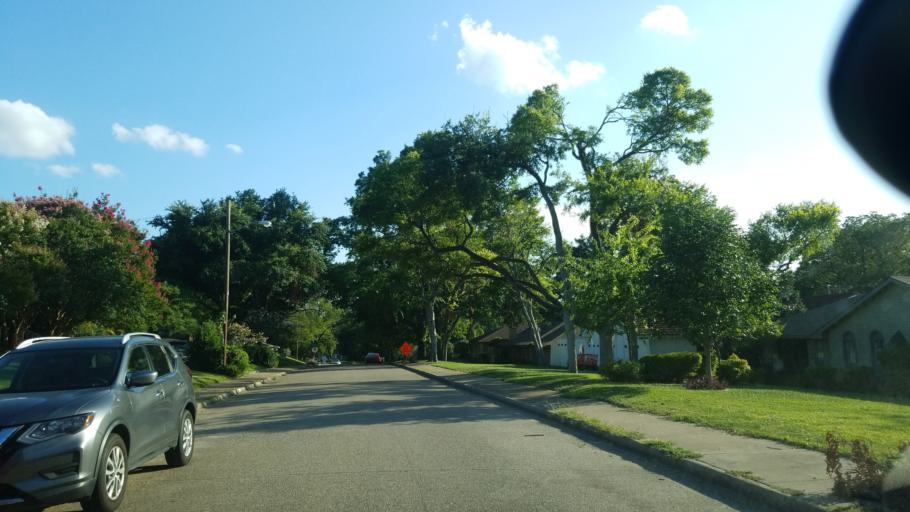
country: US
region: Texas
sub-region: Dallas County
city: Highland Park
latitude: 32.7851
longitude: -96.7119
